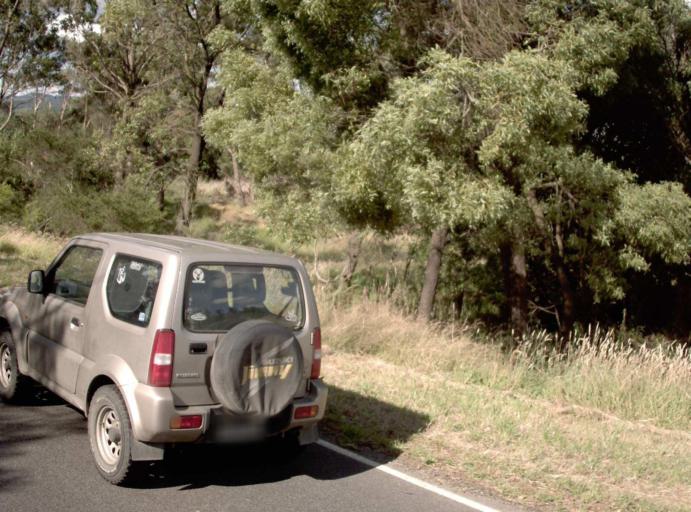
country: AU
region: Victoria
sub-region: Latrobe
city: Morwell
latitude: -38.1789
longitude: 146.4049
